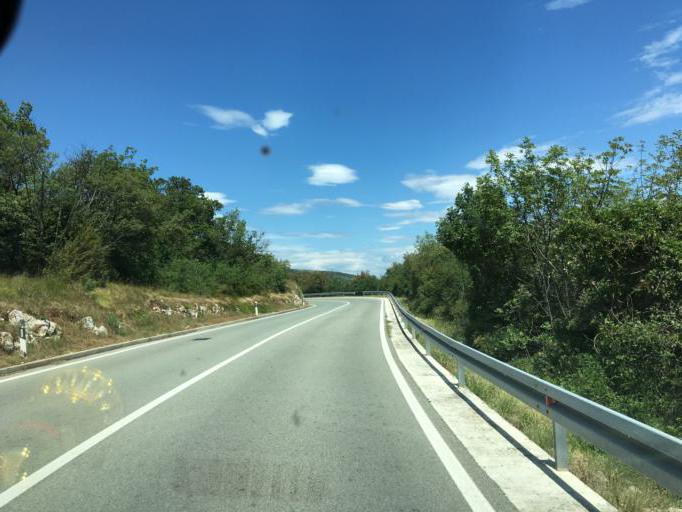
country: HR
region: Istarska
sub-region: Grad Labin
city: Rabac
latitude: 45.1438
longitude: 14.2127
